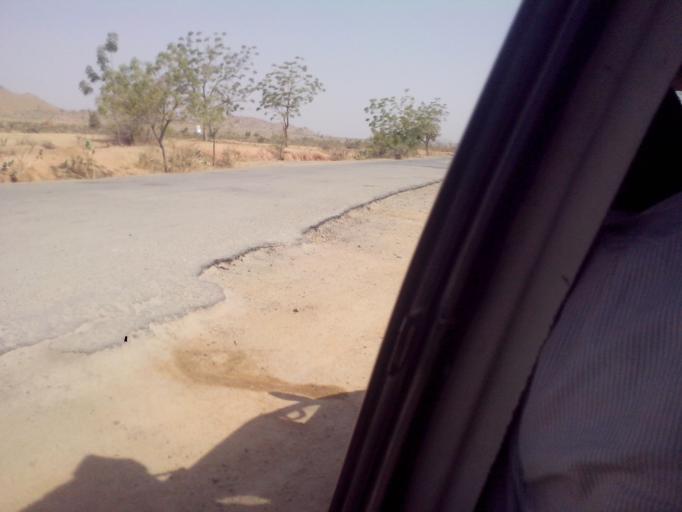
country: CM
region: Far North
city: Mora
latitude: 11.0563
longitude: 14.1514
